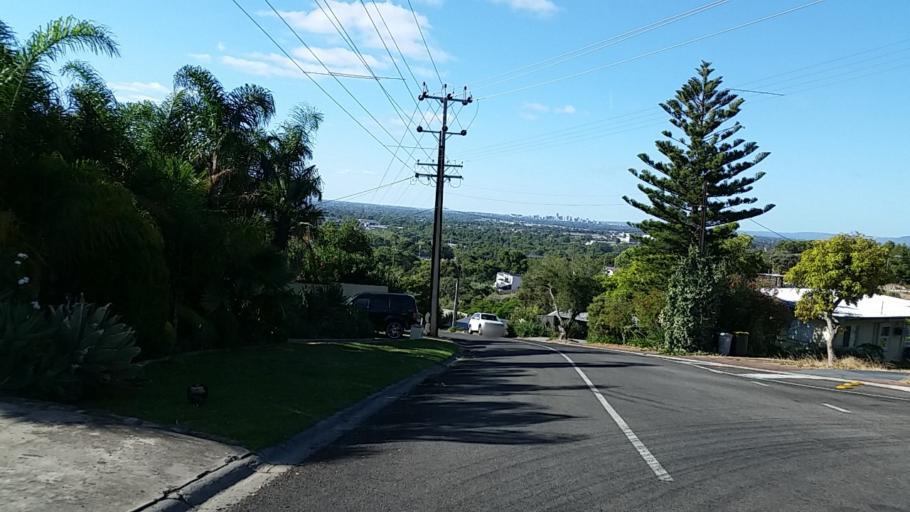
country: AU
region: South Australia
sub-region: Onkaparinga
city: Bedford Park
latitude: -35.0318
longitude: 138.5580
